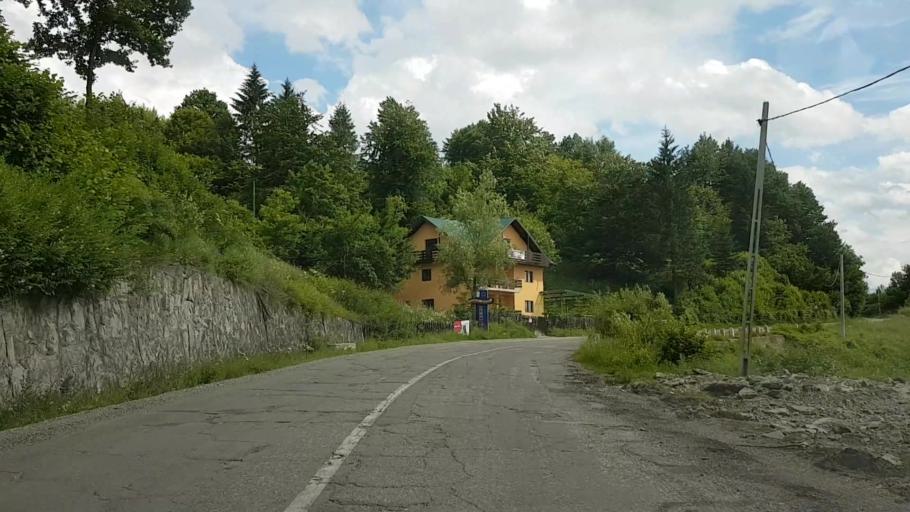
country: RO
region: Neamt
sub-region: Comuna Bicaz
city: Dodeni
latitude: 46.9901
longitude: 26.1022
